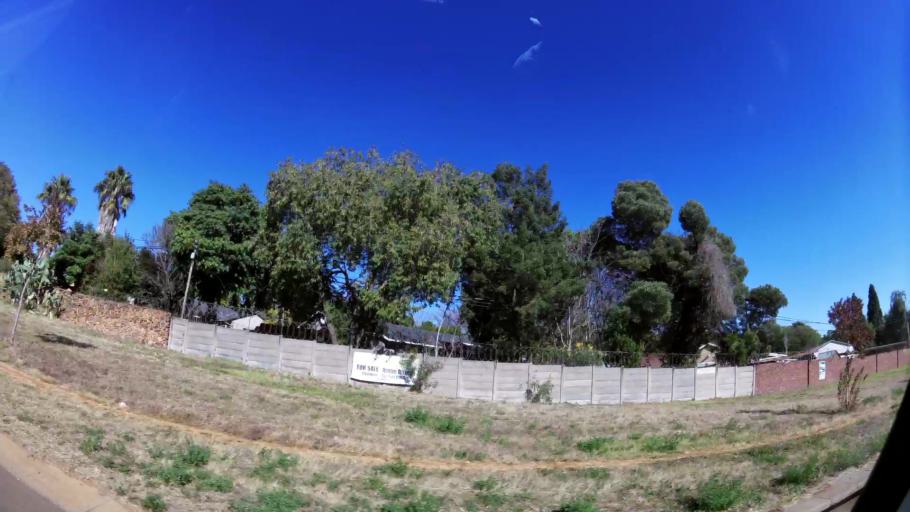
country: ZA
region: Gauteng
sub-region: City of Tshwane Metropolitan Municipality
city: Pretoria
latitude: -25.7953
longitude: 28.3137
